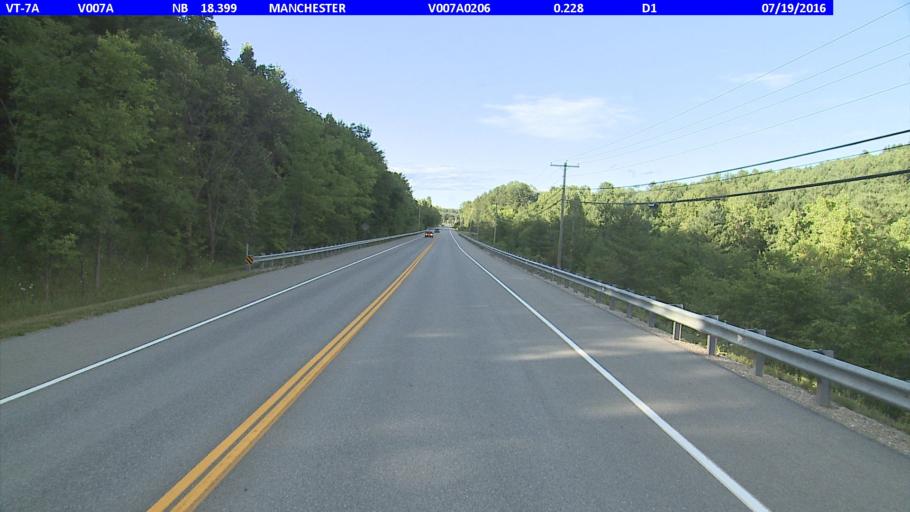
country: US
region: Vermont
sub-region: Bennington County
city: Arlington
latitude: 43.1217
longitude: -73.1015
